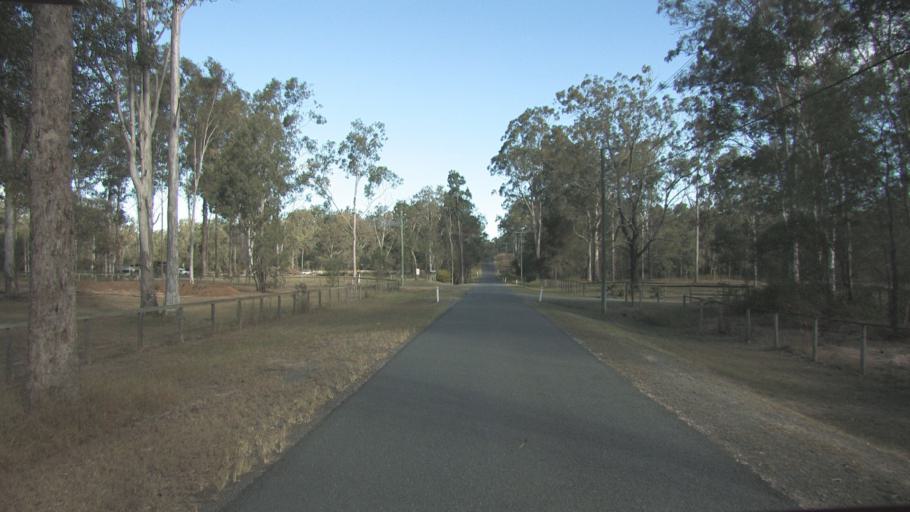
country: AU
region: Queensland
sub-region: Logan
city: North Maclean
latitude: -27.8241
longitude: 153.0629
